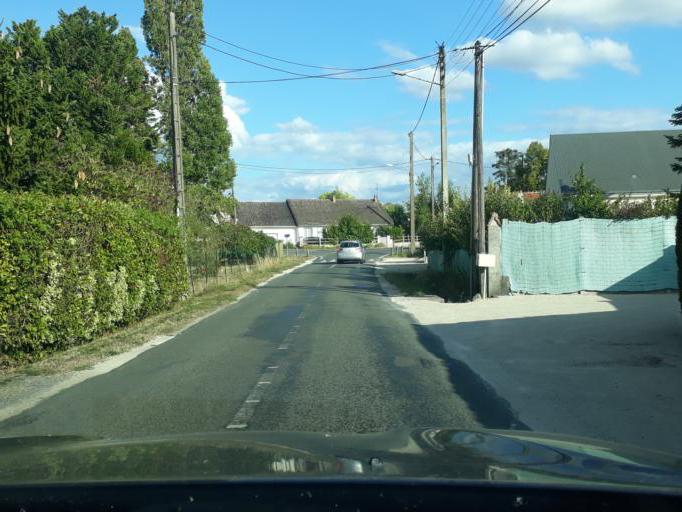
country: FR
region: Centre
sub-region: Departement du Loiret
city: Rebrechien
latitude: 47.9860
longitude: 2.0332
